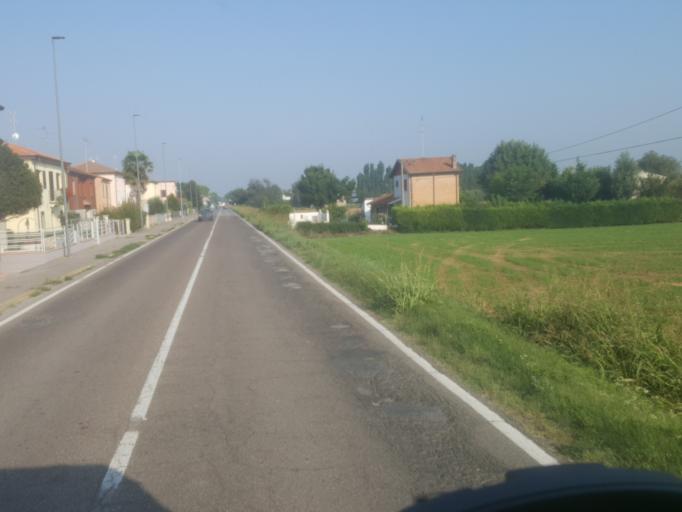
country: IT
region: Emilia-Romagna
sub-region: Provincia di Ravenna
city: Mezzano
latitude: 44.4565
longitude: 12.1045
